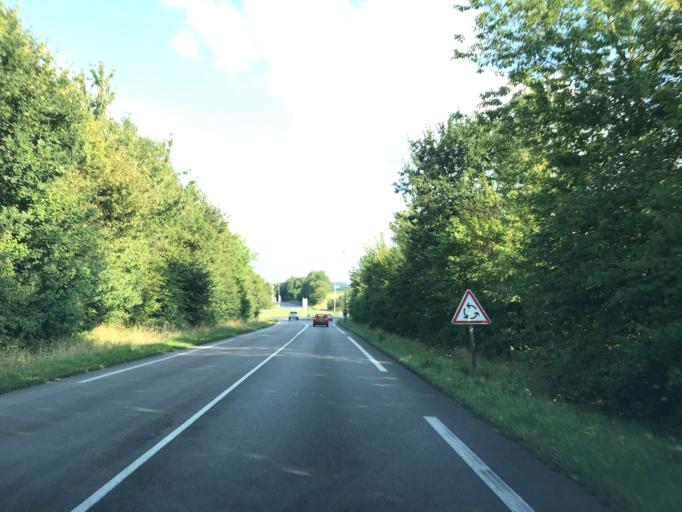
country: FR
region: Haute-Normandie
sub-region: Departement de la Seine-Maritime
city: Bolbec
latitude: 49.5756
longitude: 0.4557
